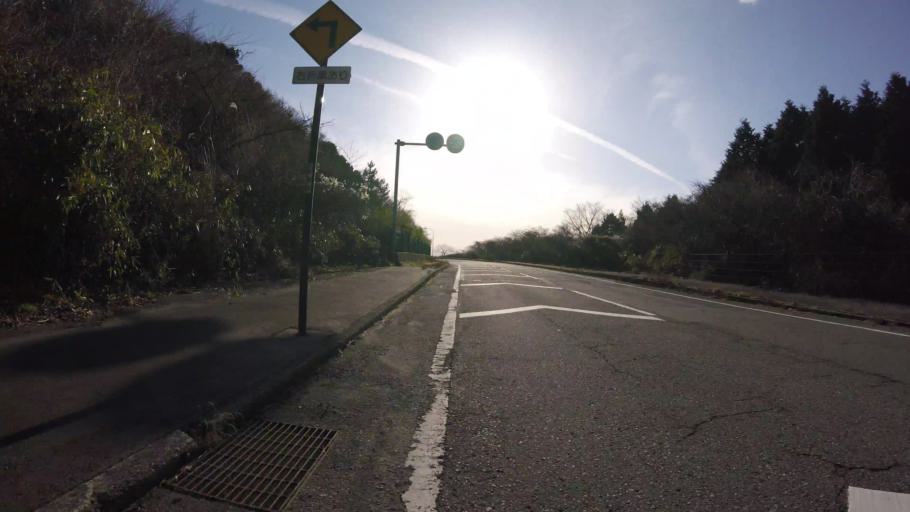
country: JP
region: Kanagawa
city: Hakone
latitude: 35.1721
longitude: 139.0213
